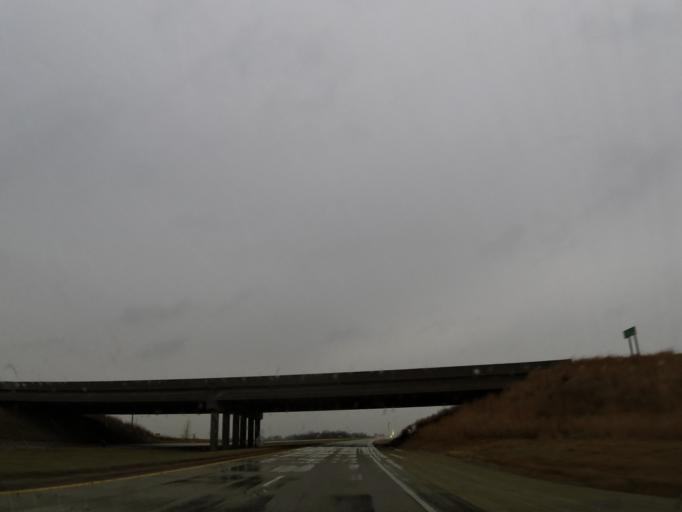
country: US
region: Iowa
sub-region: Cerro Gordo County
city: Mason City
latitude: 43.1046
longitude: -93.2004
